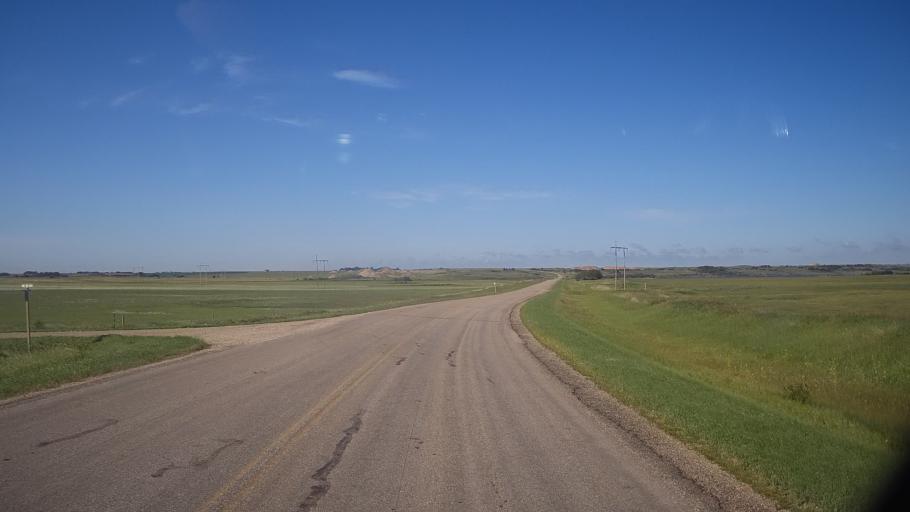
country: CA
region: Saskatchewan
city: Watrous
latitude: 51.7201
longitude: -105.3590
